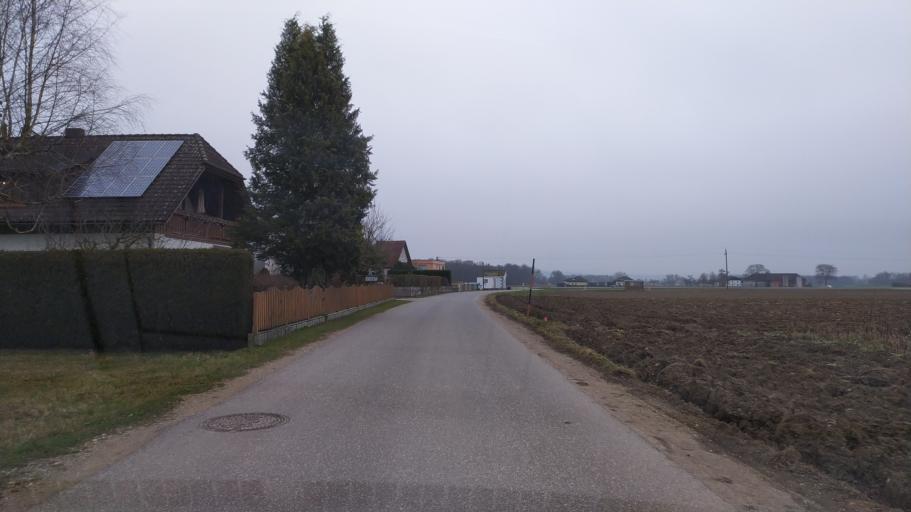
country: AT
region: Upper Austria
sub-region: Politischer Bezirk Perg
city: Perg
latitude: 48.2058
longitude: 14.7153
